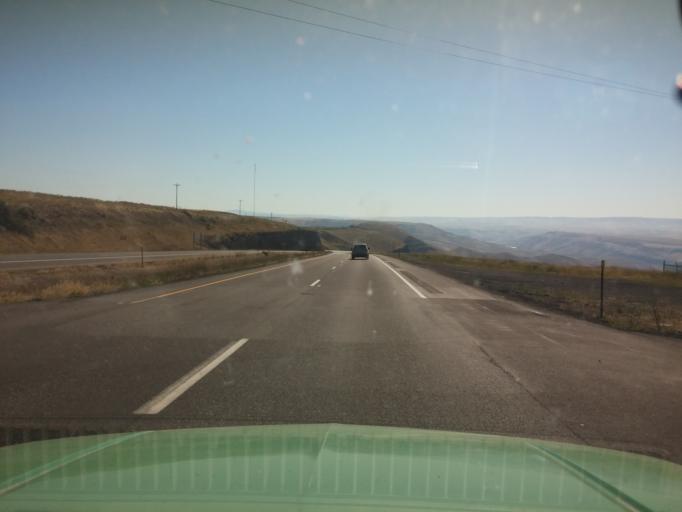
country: US
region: Idaho
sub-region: Nez Perce County
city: Lewiston
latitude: 46.4620
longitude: -117.0091
